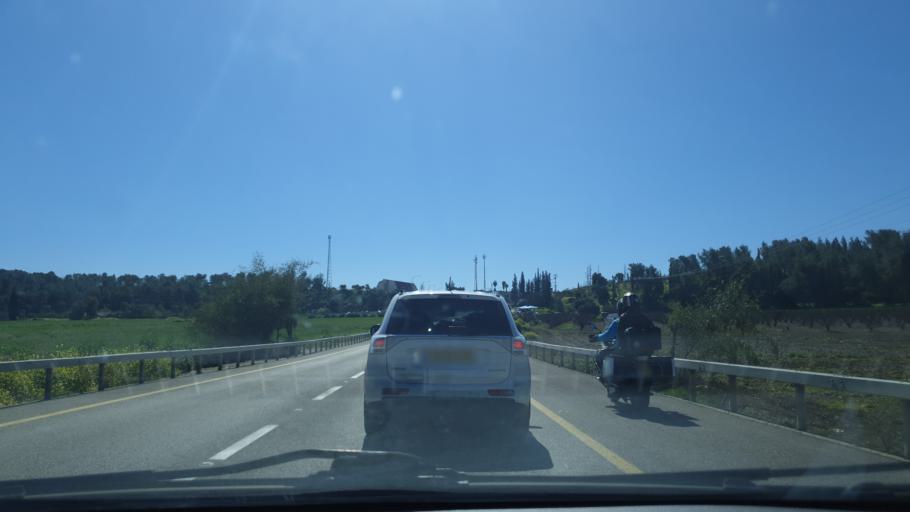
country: IL
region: Jerusalem
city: Bet Shemesh
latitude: 31.6906
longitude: 34.9444
